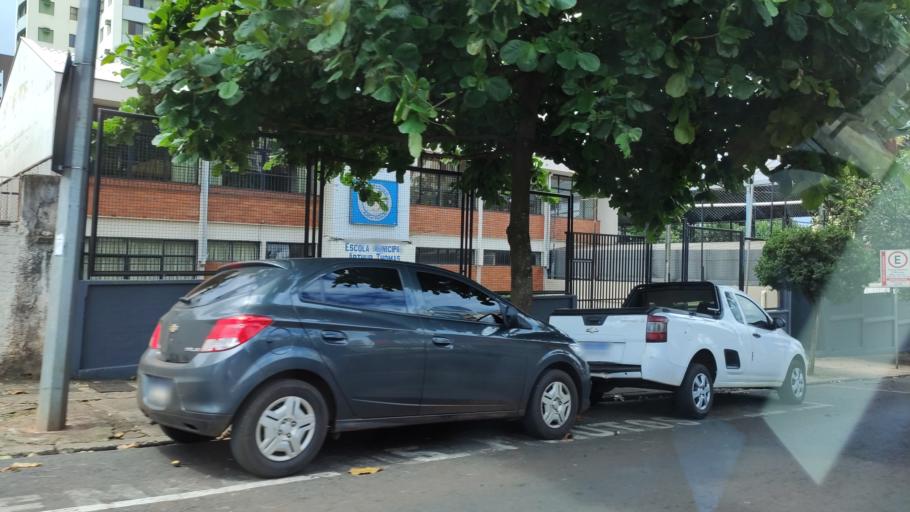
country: BR
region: Parana
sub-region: Londrina
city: Londrina
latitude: -23.3155
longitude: -51.1569
